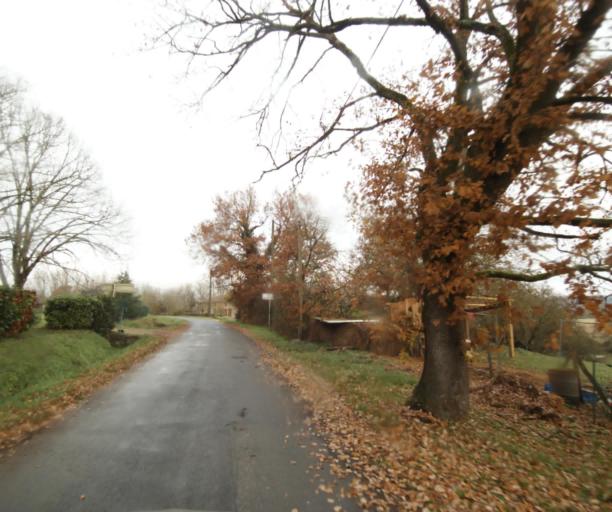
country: FR
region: Midi-Pyrenees
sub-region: Departement du Tarn-et-Garonne
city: Nohic
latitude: 43.8783
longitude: 1.4649
